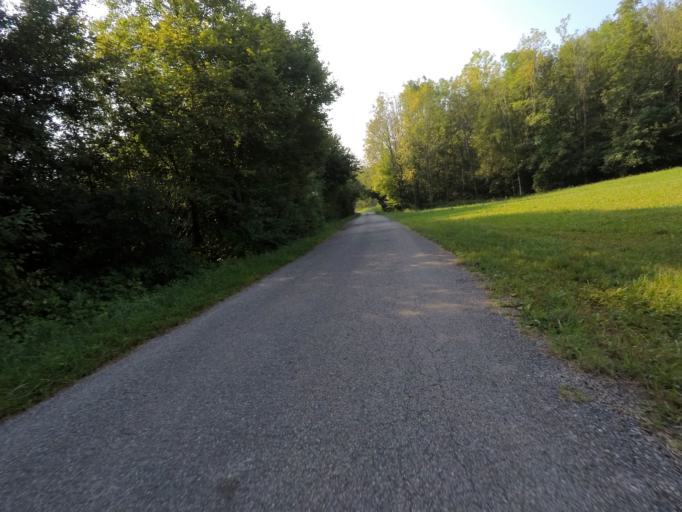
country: IT
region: Friuli Venezia Giulia
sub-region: Provincia di Pordenone
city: Pinzano al Tagliamento
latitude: 46.2035
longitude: 12.9525
